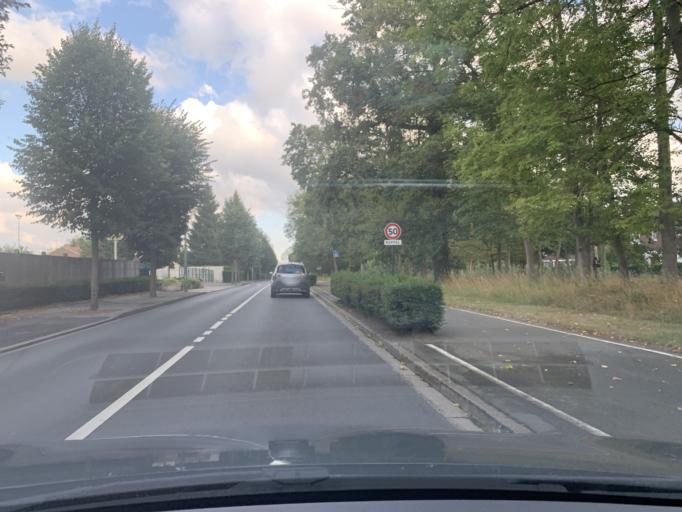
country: FR
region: Nord-Pas-de-Calais
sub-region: Departement du Pas-de-Calais
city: Libercourt
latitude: 50.4853
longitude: 2.9980
